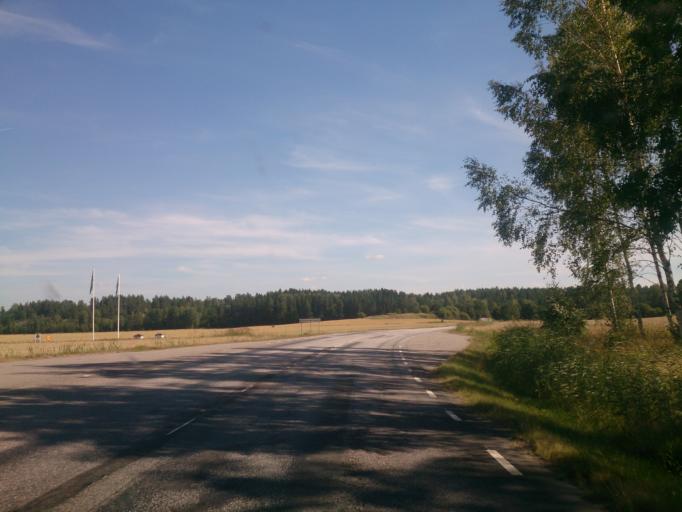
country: SE
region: OEstergoetland
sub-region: Norrkopings Kommun
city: Norrkoping
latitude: 58.4936
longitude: 16.1270
